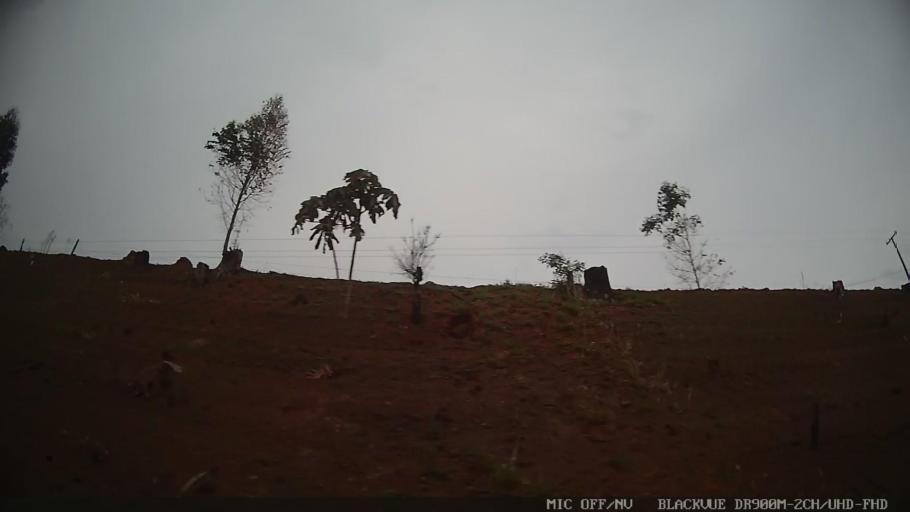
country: BR
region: Sao Paulo
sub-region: Braganca Paulista
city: Braganca Paulista
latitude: -22.9552
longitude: -46.6058
